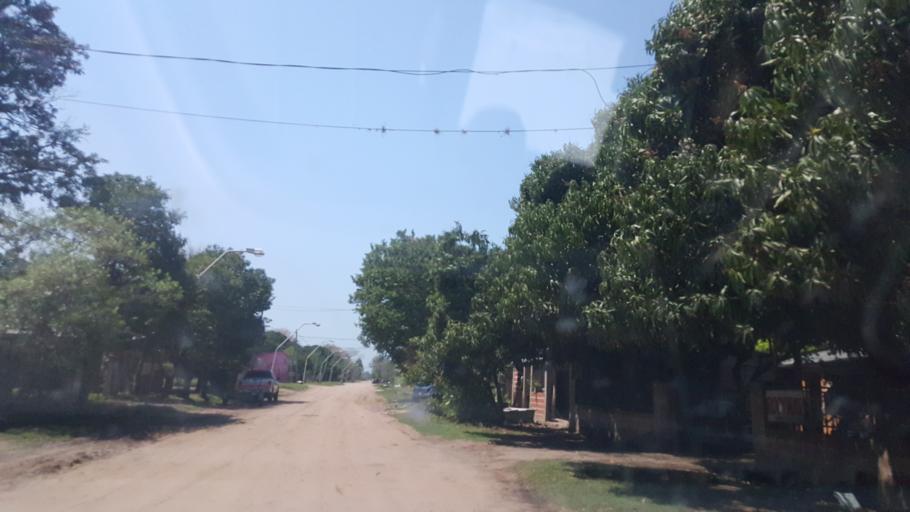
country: AR
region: Corrientes
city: Ita Ibate
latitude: -27.4233
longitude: -57.3326
